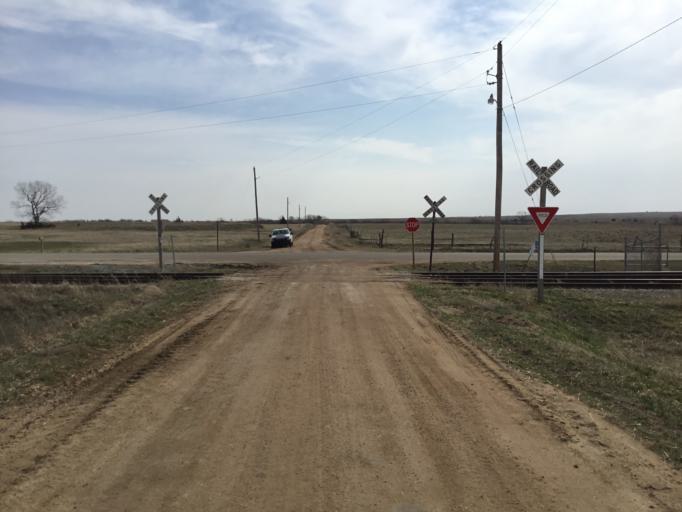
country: US
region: Kansas
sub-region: Ellsworth County
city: Ellsworth
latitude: 38.7252
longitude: -98.1272
